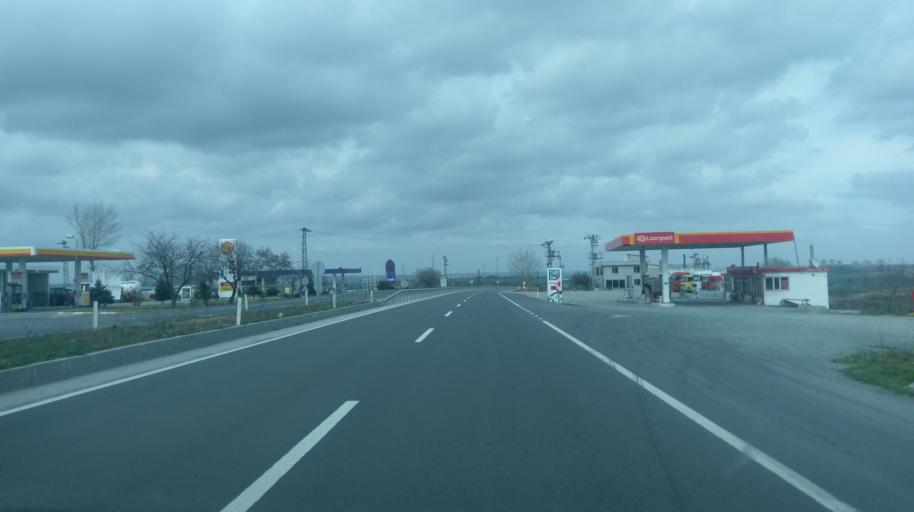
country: TR
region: Edirne
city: Uzun Keupru
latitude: 41.2108
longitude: 26.6802
